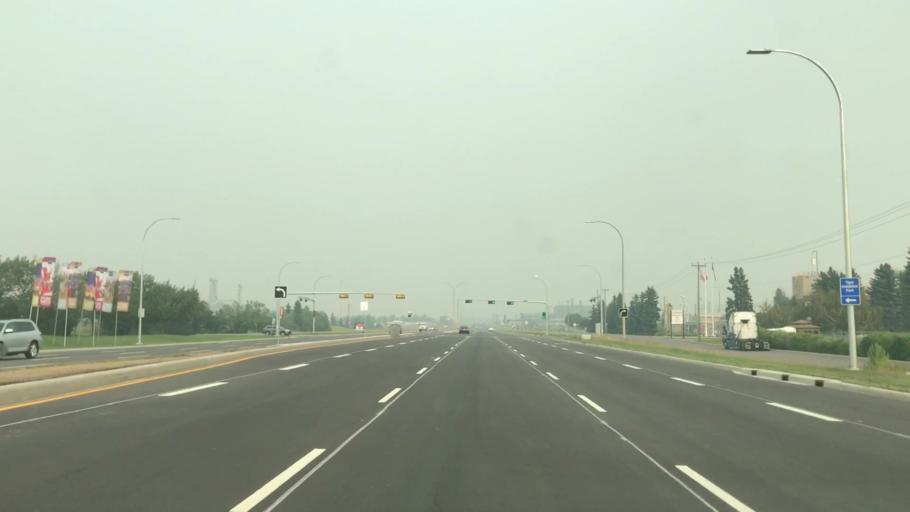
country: CA
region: Alberta
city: Edmonton
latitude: 53.5420
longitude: -113.4124
